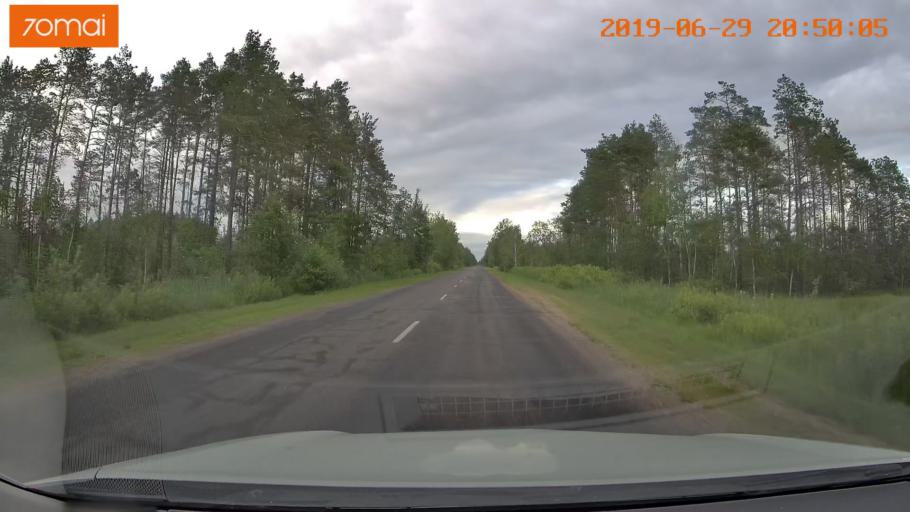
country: BY
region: Brest
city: Hantsavichy
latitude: 52.6724
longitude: 26.3310
